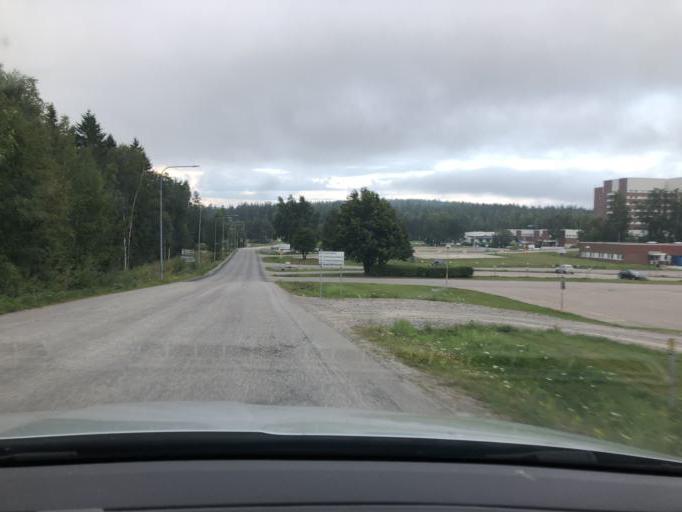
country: SE
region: Vaesternorrland
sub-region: Sundsvalls Kommun
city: Sundsvall
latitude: 62.4066
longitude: 17.3014
